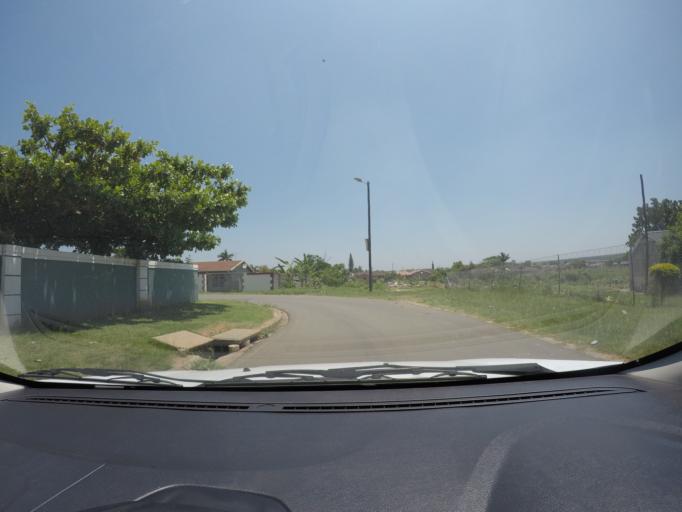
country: ZA
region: KwaZulu-Natal
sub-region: uThungulu District Municipality
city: eSikhawini
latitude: -28.8846
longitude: 31.8956
